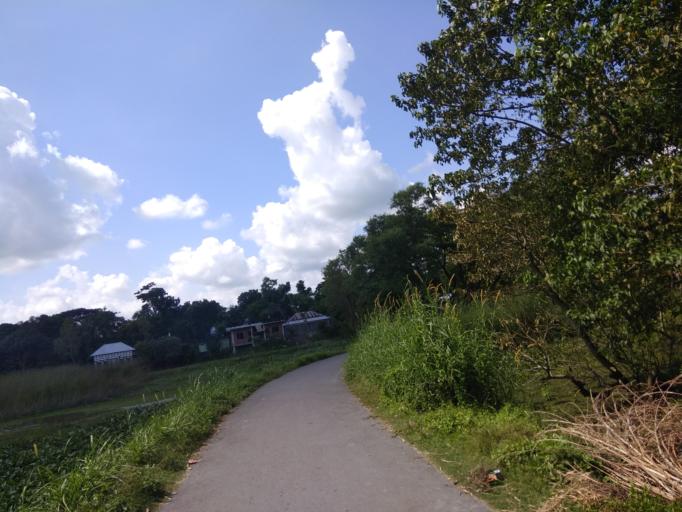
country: BD
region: Dhaka
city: Narayanganj
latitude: 23.4417
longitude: 90.4751
